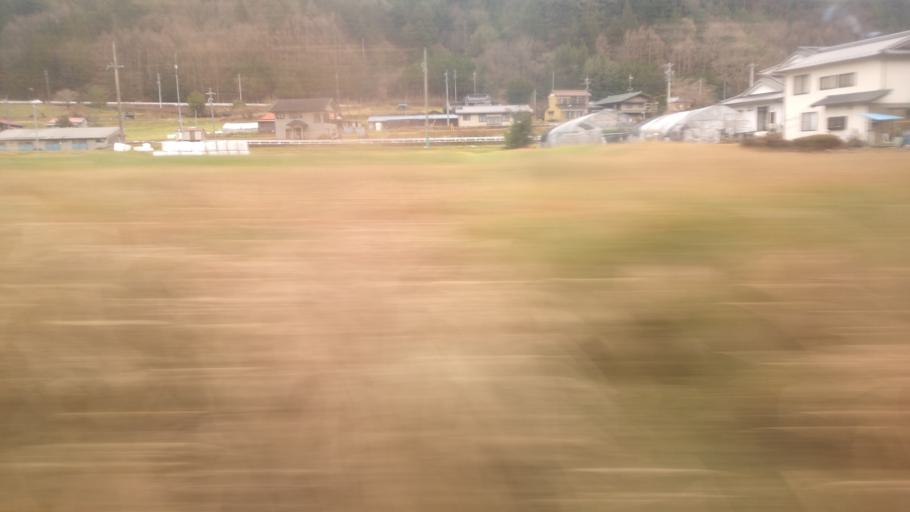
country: JP
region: Nagano
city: Ina
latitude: 35.8753
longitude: 137.7483
